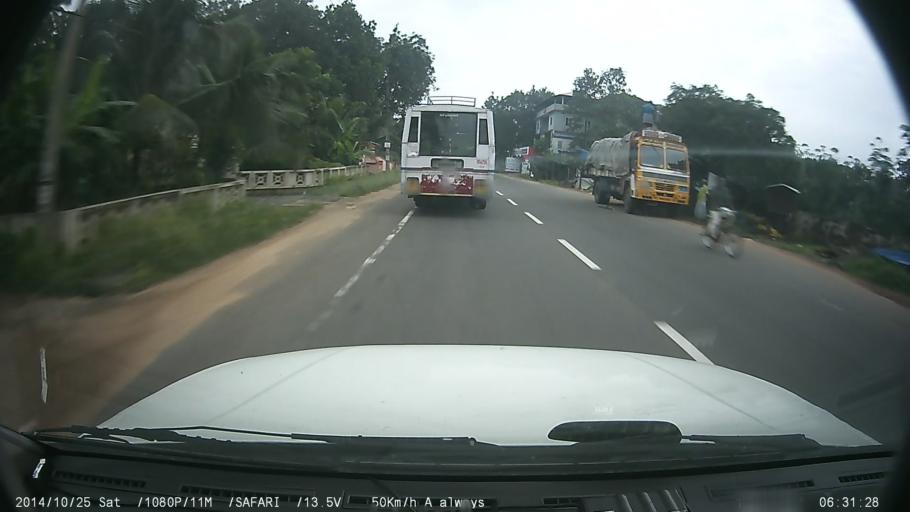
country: IN
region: Kerala
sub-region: Ernakulam
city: Muvattupula
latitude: 10.0270
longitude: 76.5532
